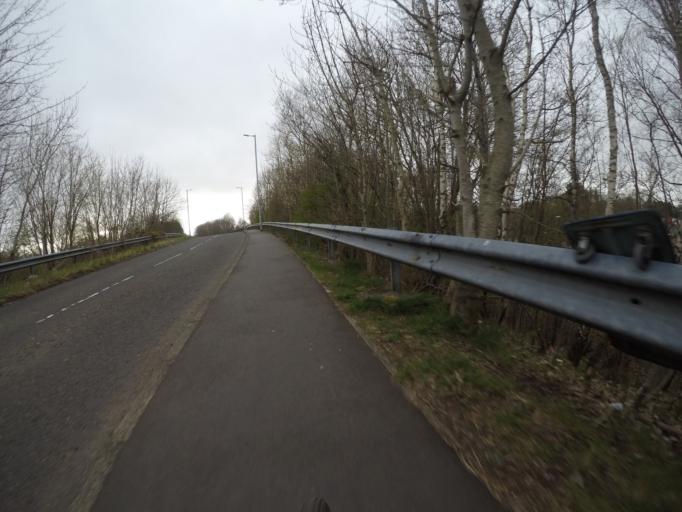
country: GB
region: Scotland
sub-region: North Ayrshire
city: Irvine
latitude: 55.6150
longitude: -4.6440
